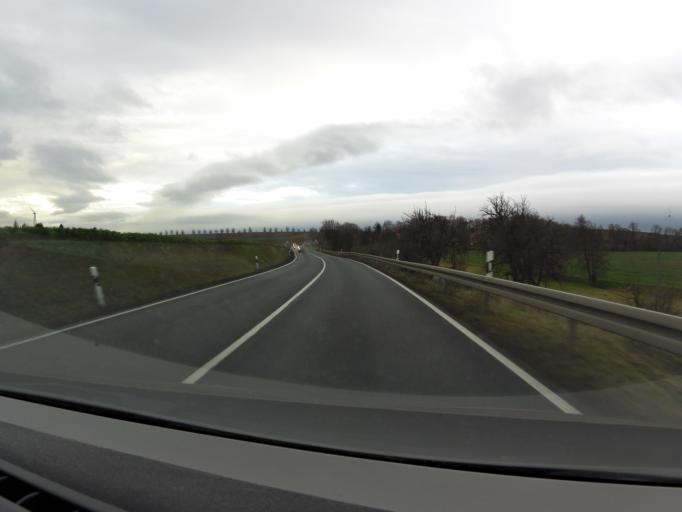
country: DE
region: Saxony-Anhalt
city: Hettstedt
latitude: 51.6848
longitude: 11.4556
